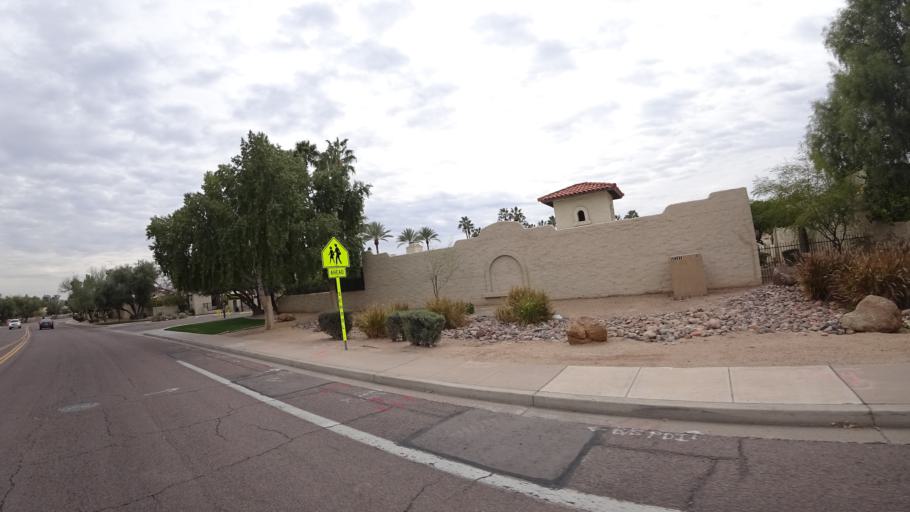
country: US
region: Arizona
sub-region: Maricopa County
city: Glendale
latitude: 33.6377
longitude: -112.1213
